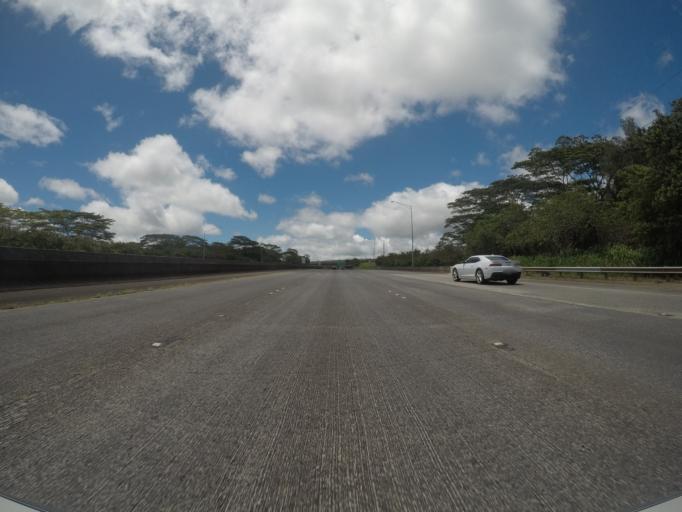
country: US
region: Hawaii
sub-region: Honolulu County
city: Mililani Town
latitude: 21.4492
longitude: -157.9905
